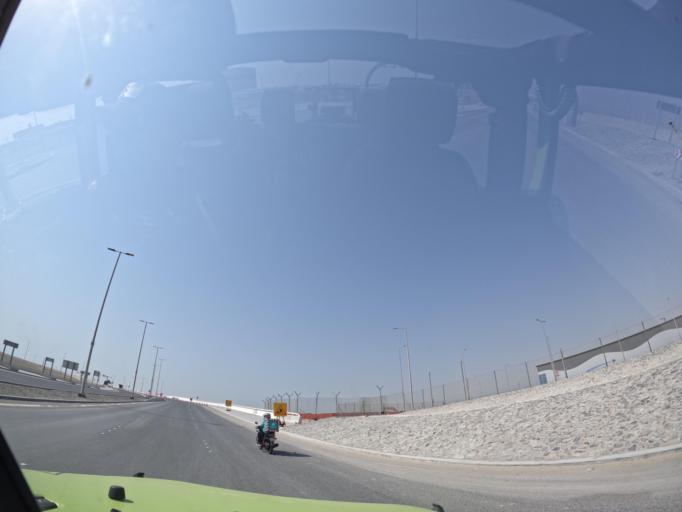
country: AE
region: Abu Dhabi
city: Abu Dhabi
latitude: 24.4628
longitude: 54.6319
